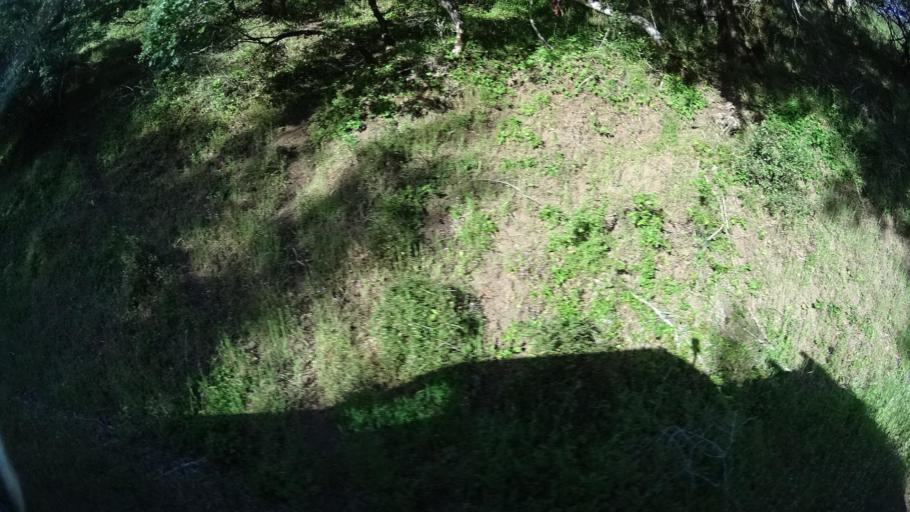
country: US
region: California
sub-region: Lake County
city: Upper Lake
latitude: 39.1384
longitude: -123.0003
